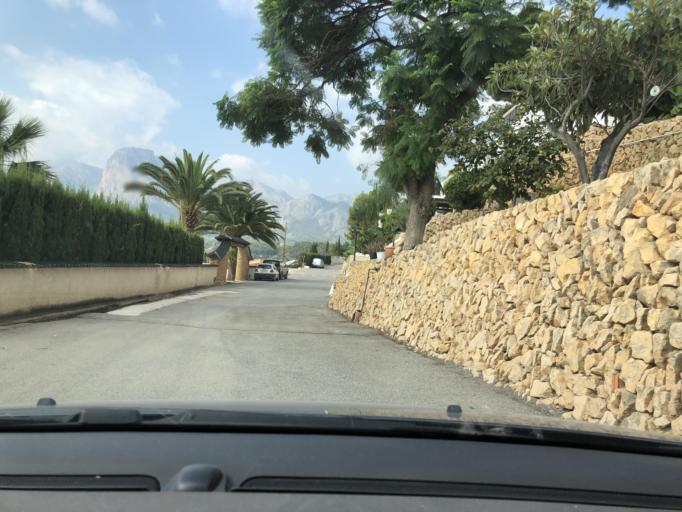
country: ES
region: Valencia
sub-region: Provincia de Alicante
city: Callosa d'En Sarria
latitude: 38.6326
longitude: -0.1084
